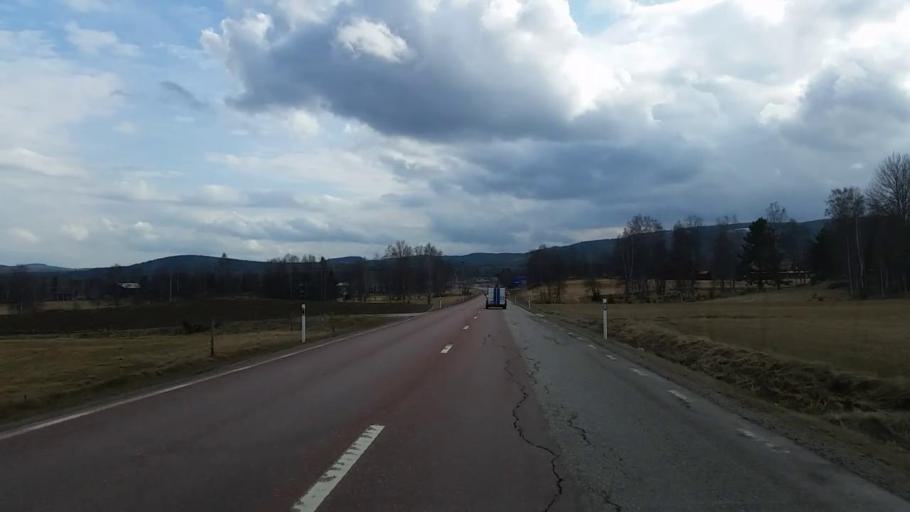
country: SE
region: Gaevleborg
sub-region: Ljusdals Kommun
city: Jaervsoe
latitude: 61.6791
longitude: 16.1453
